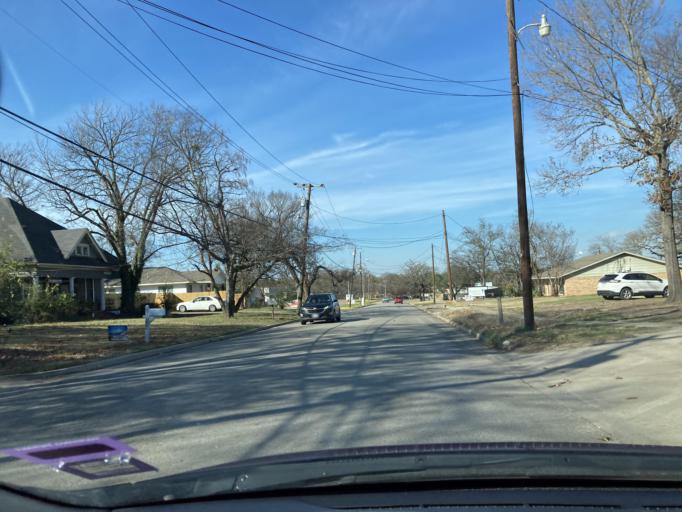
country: US
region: Texas
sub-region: Navarro County
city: Corsicana
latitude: 32.0976
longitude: -96.4708
